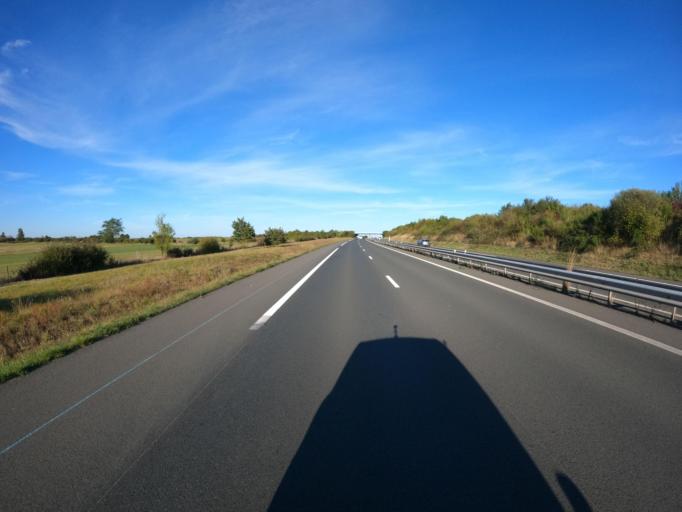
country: FR
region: Pays de la Loire
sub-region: Departement de Maine-et-Loire
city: Chemille-Melay
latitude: 47.2343
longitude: -0.7461
